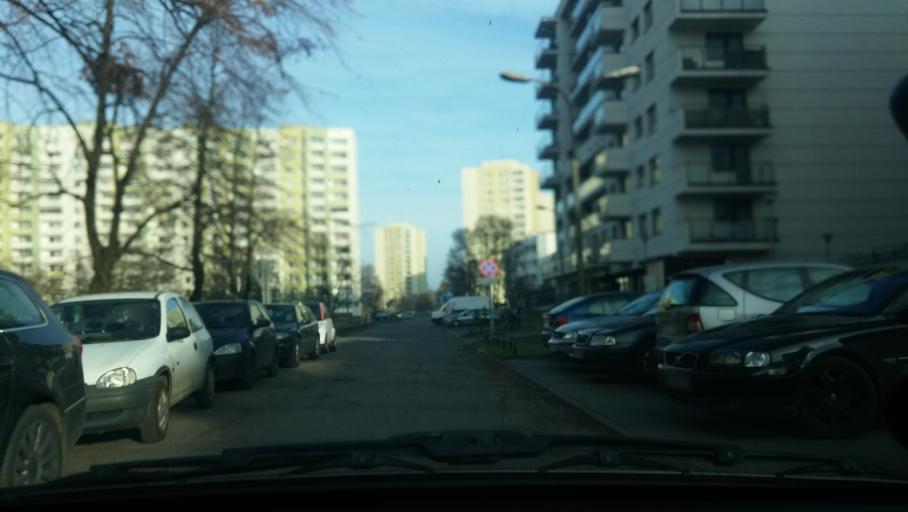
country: PL
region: Masovian Voivodeship
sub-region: Warszawa
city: Praga Poludnie
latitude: 52.2357
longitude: 21.1113
